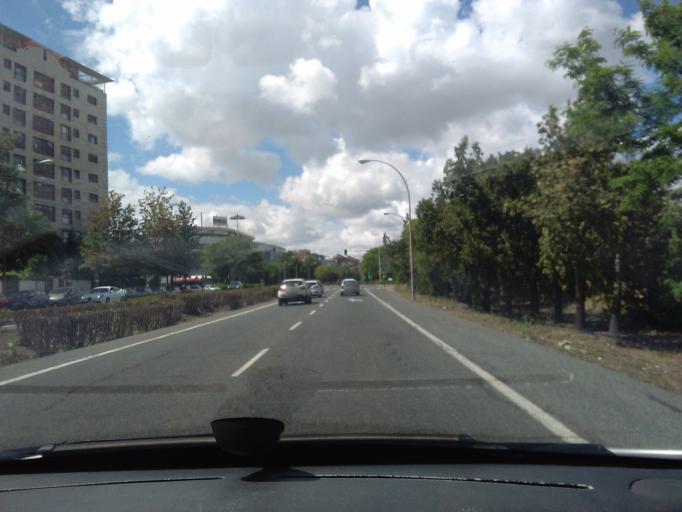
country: ES
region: Andalusia
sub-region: Provincia de Sevilla
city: Sevilla
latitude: 37.3453
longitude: -5.9748
